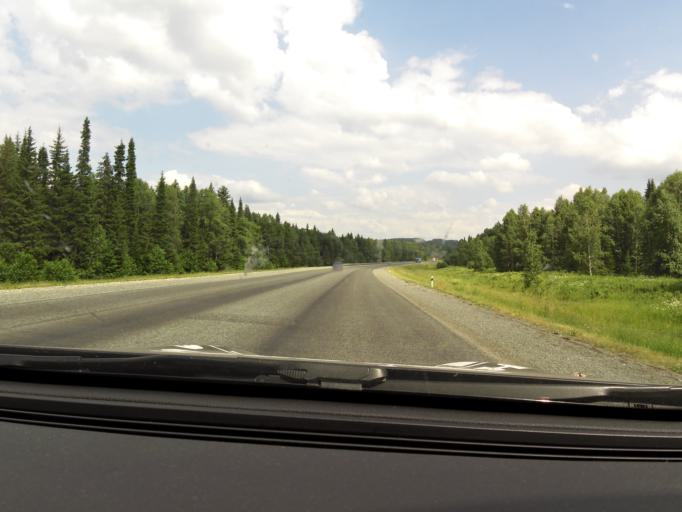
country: RU
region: Sverdlovsk
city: Ufimskiy
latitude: 56.7870
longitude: 58.3766
